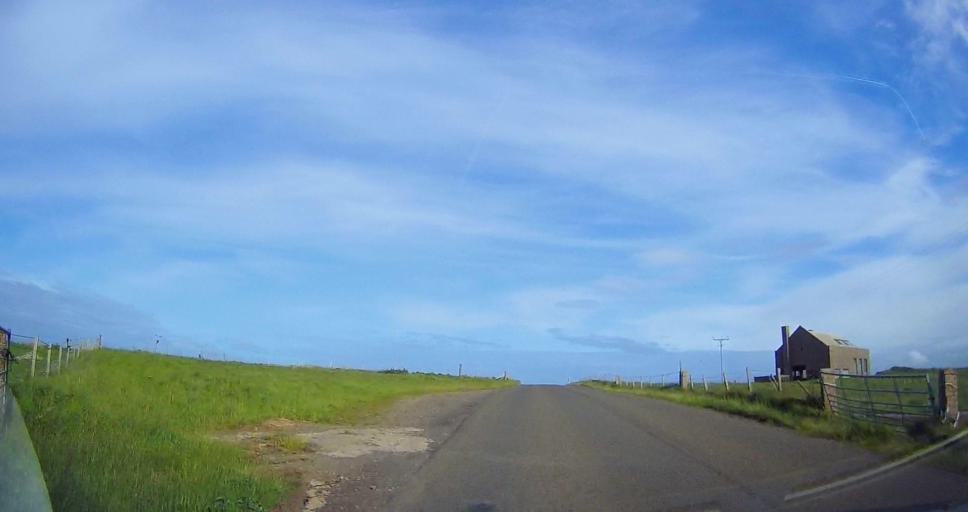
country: GB
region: Scotland
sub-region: Orkney Islands
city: Stromness
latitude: 58.8237
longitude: -3.2093
